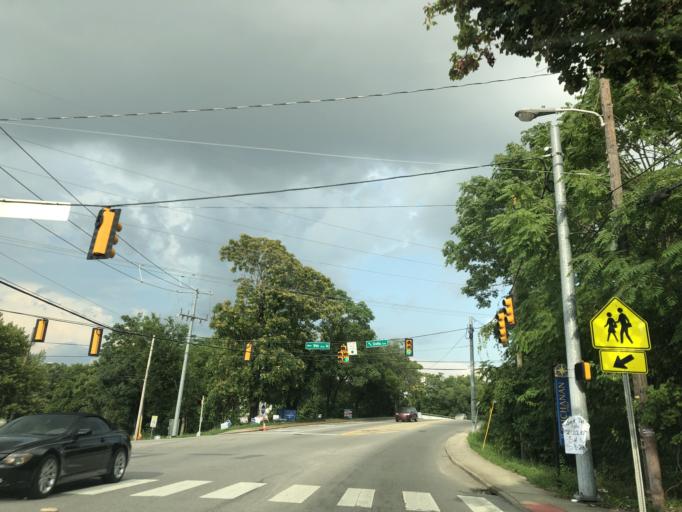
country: US
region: Tennessee
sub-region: Davidson County
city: Nashville
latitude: 36.1805
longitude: -86.8019
